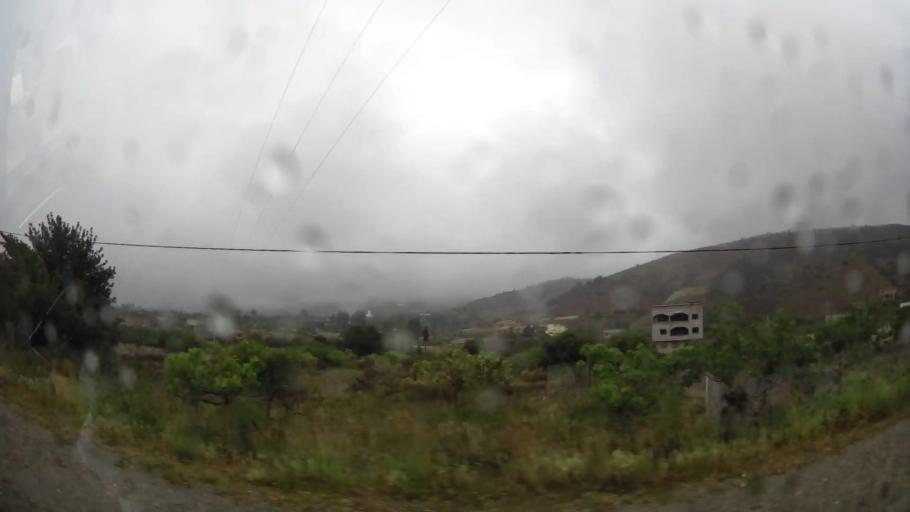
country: MA
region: Taza-Al Hoceima-Taounate
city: Imzourene
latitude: 35.1346
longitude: -3.7823
